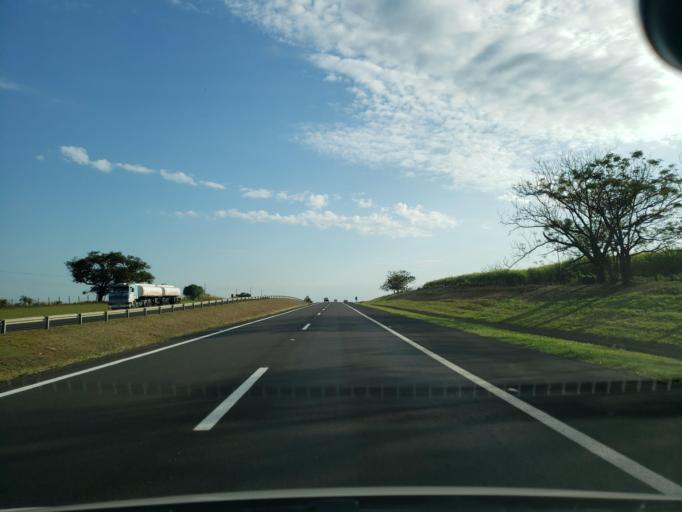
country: BR
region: Sao Paulo
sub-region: Valparaiso
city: Valparaiso
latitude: -21.2072
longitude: -50.8166
